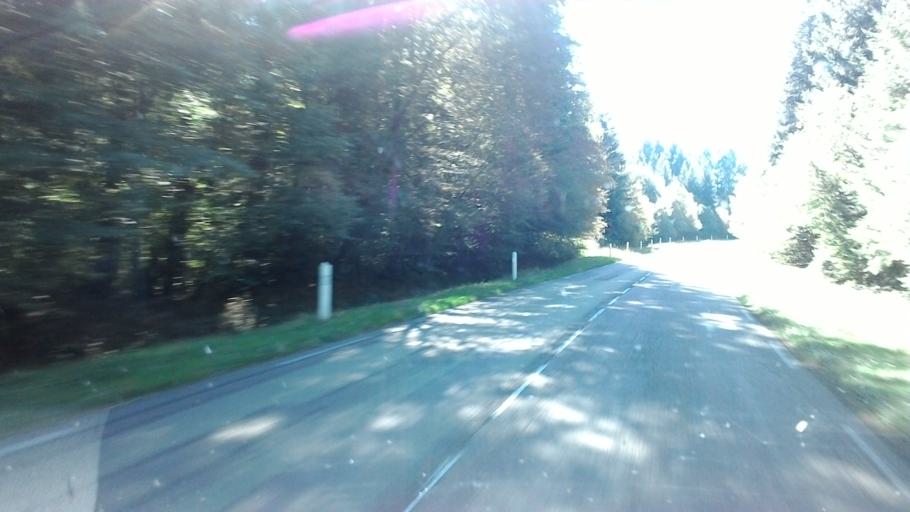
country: FR
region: Bourgogne
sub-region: Departement de la Cote-d'Or
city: Saulieu
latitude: 47.3283
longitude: 4.2721
